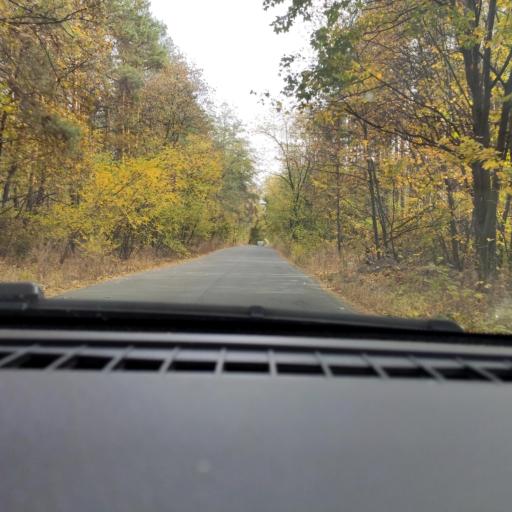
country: RU
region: Voronezj
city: Somovo
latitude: 51.6876
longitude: 39.2949
